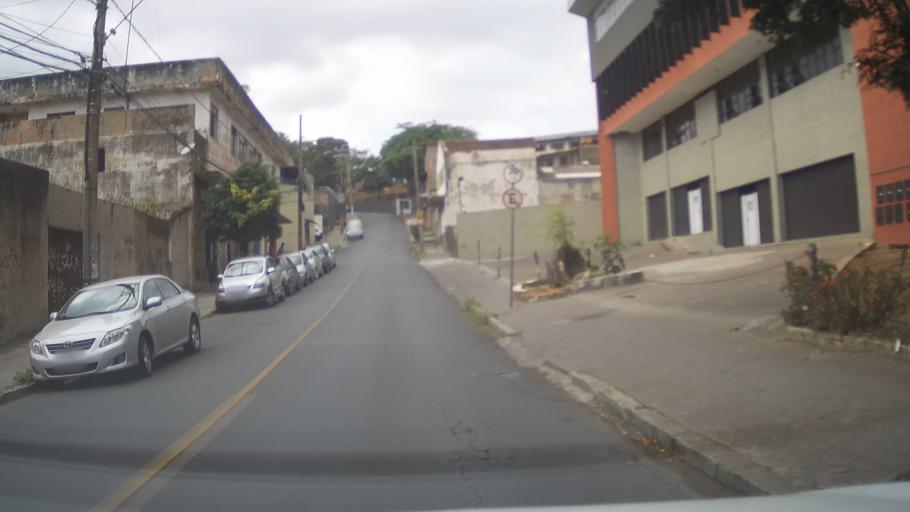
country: BR
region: Minas Gerais
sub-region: Belo Horizonte
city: Belo Horizonte
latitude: -19.8972
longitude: -43.9463
